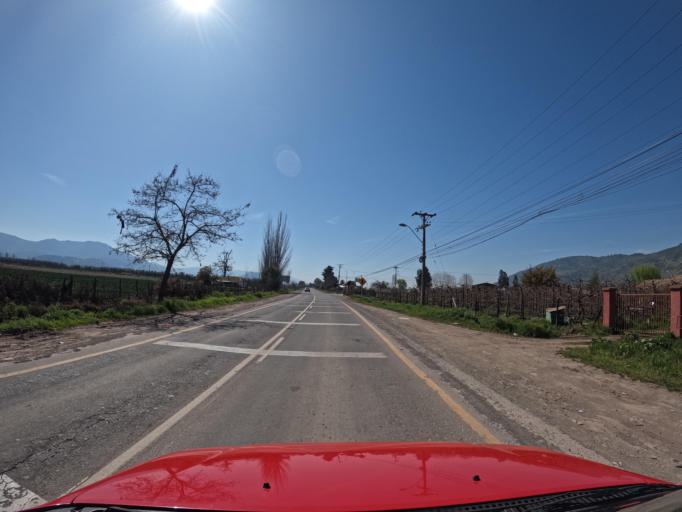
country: CL
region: Maule
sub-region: Provincia de Curico
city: Rauco
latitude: -35.0209
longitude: -71.4290
